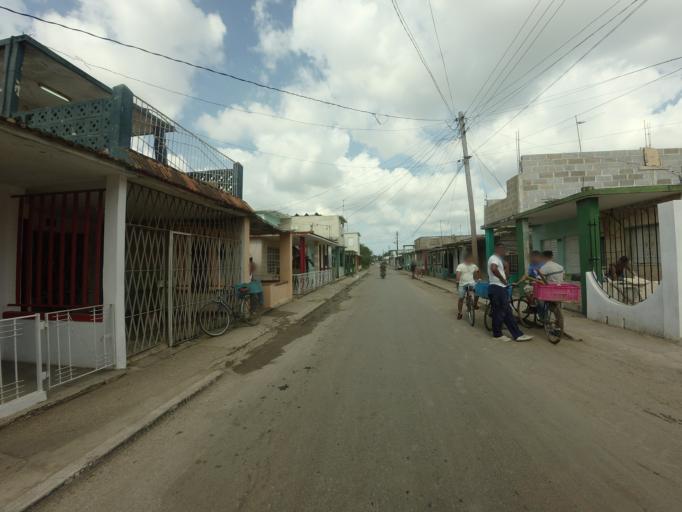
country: CU
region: Artemisa
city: Bauta
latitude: 22.9813
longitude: -82.5506
